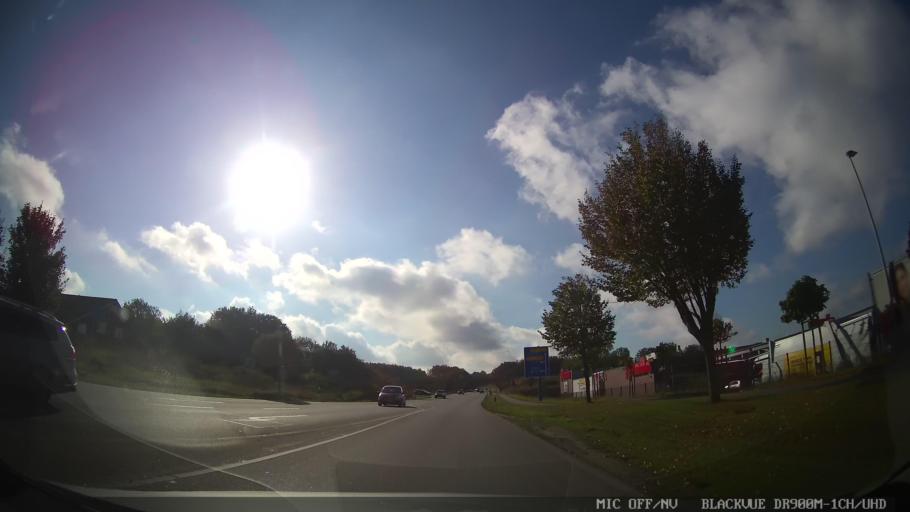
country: DE
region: Schleswig-Holstein
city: Heiligenhafen
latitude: 54.3645
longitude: 11.0093
